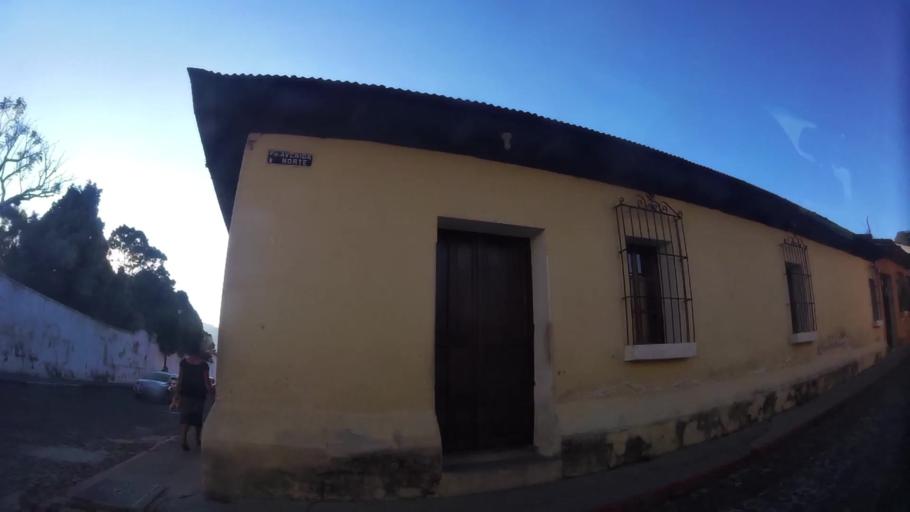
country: GT
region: Sacatepequez
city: Antigua Guatemala
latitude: 14.5595
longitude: -90.7296
